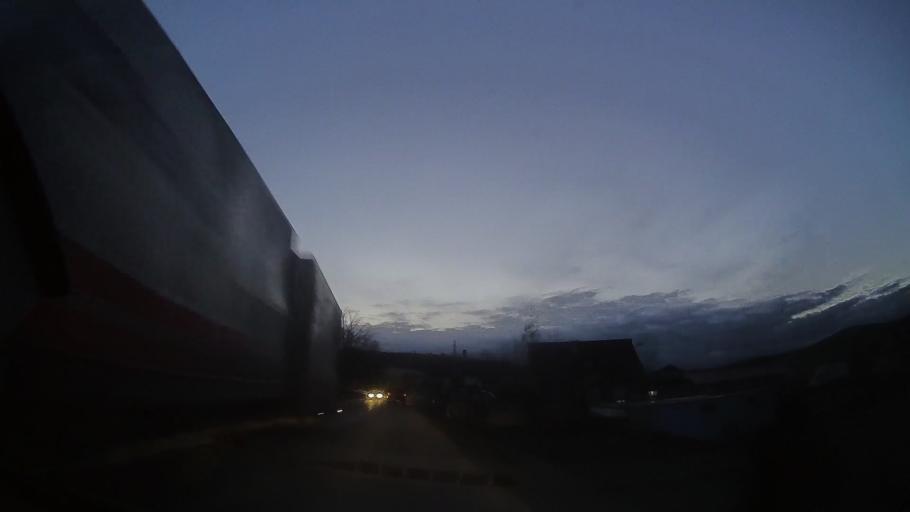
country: RO
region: Mures
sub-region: Comuna Sarmasu
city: Sarmasu
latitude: 46.7587
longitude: 24.1718
